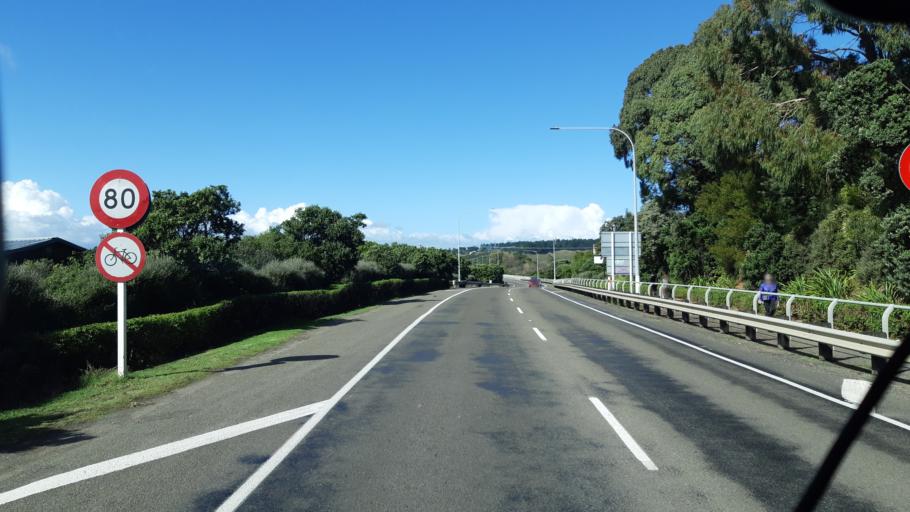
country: NZ
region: Manawatu-Wanganui
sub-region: Wanganui District
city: Wanganui
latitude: -39.9424
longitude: 175.0432
